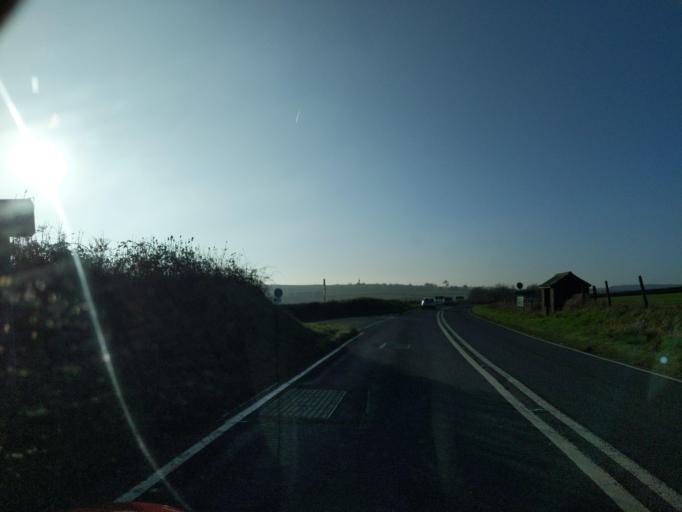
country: GB
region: England
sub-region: Cornwall
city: Liskeard
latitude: 50.4513
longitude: -4.5401
